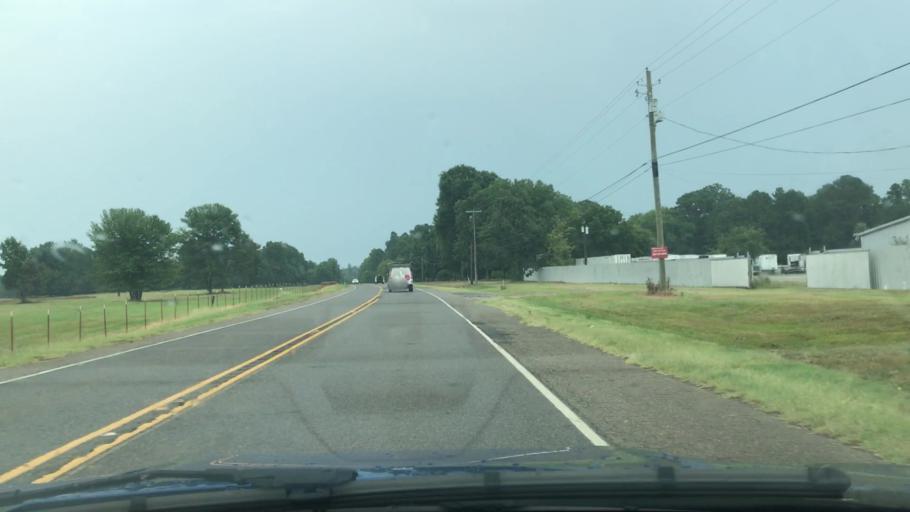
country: US
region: Texas
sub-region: Harrison County
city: Waskom
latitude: 32.4611
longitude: -94.0271
